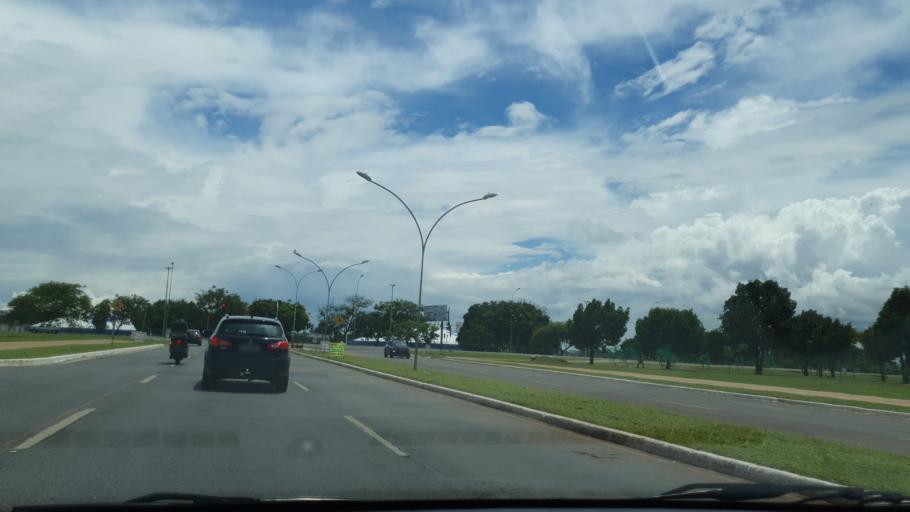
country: BR
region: Federal District
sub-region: Brasilia
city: Brasilia
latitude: -15.7833
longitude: -47.9159
